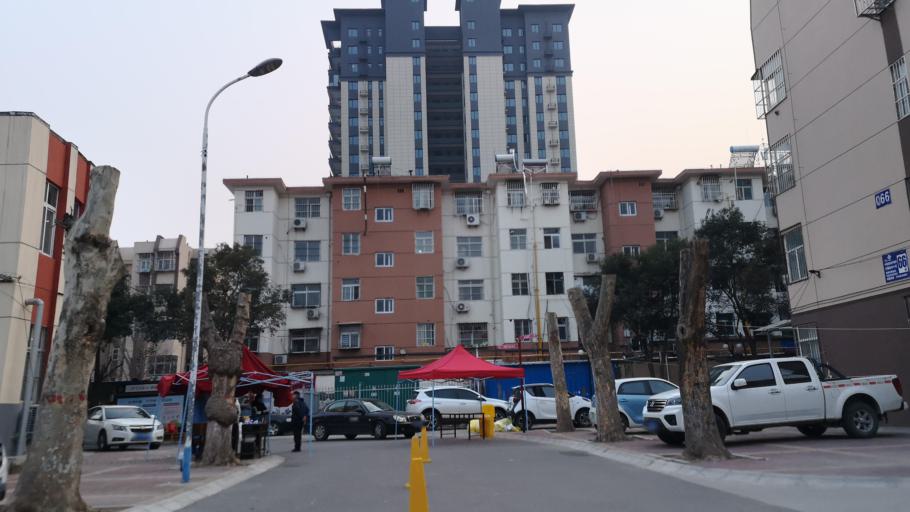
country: CN
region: Henan Sheng
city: Zhongyuanlu
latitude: 35.7836
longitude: 115.0730
